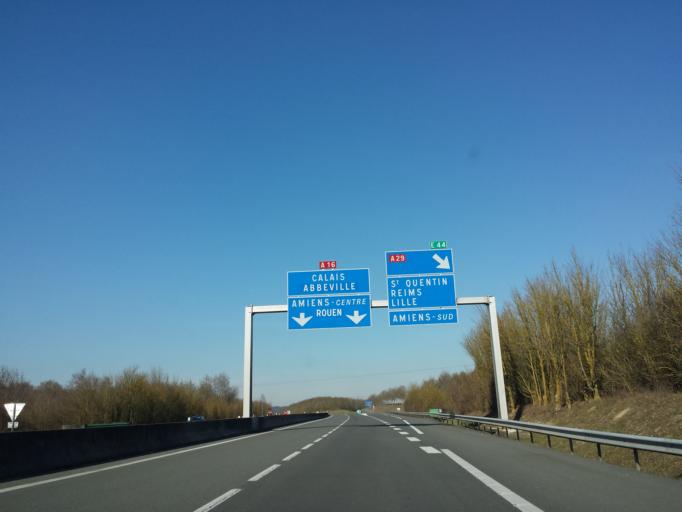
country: FR
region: Picardie
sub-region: Departement de la Somme
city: Saleux
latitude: 49.8440
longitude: 2.2465
